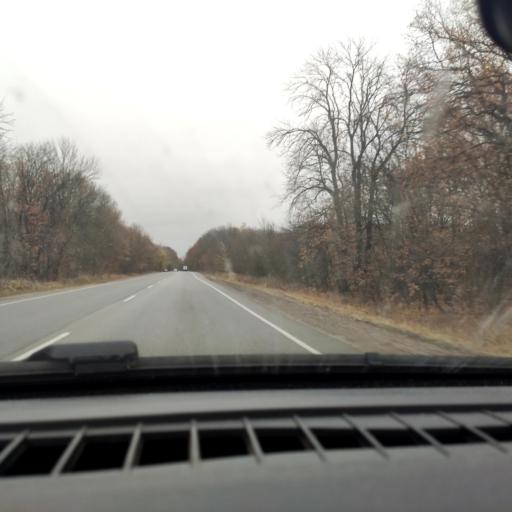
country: RU
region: Voronezj
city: Devitsa
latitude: 51.6274
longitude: 38.9900
